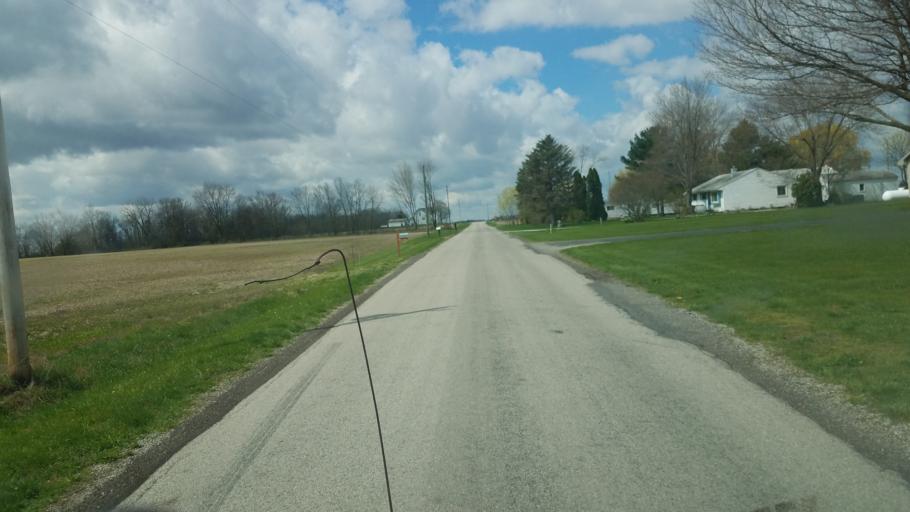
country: US
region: Ohio
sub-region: Union County
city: Richwood
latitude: 40.3947
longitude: -83.2867
